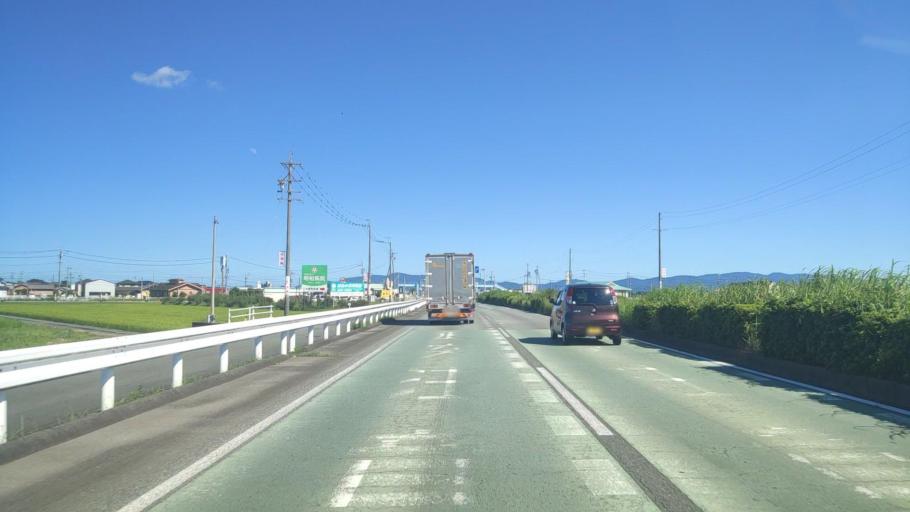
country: JP
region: Mie
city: Ise
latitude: 34.5702
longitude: 136.6318
